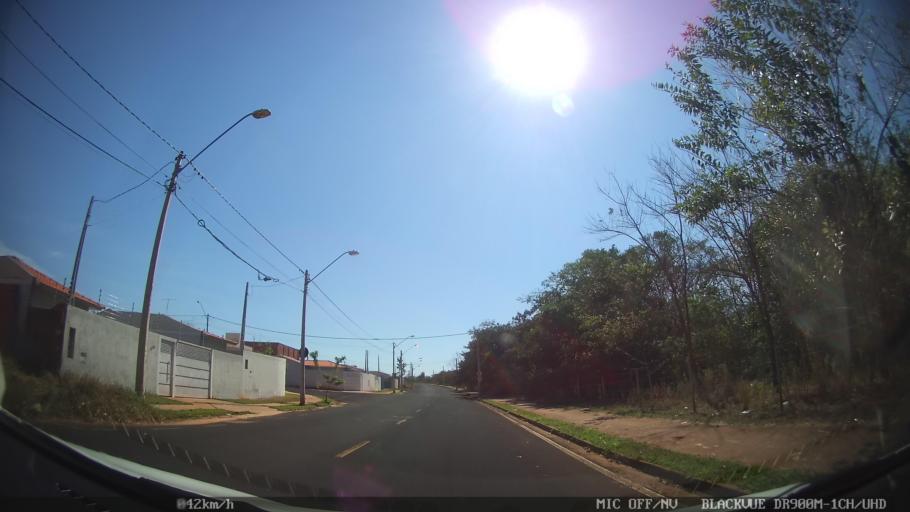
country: BR
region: Sao Paulo
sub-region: Sao Jose Do Rio Preto
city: Sao Jose do Rio Preto
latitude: -20.7584
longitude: -49.4205
